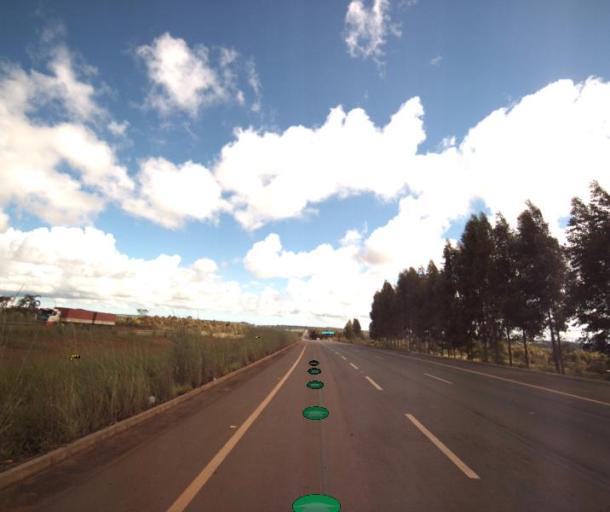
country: BR
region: Goias
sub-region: Anapolis
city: Anapolis
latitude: -16.2291
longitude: -49.0094
